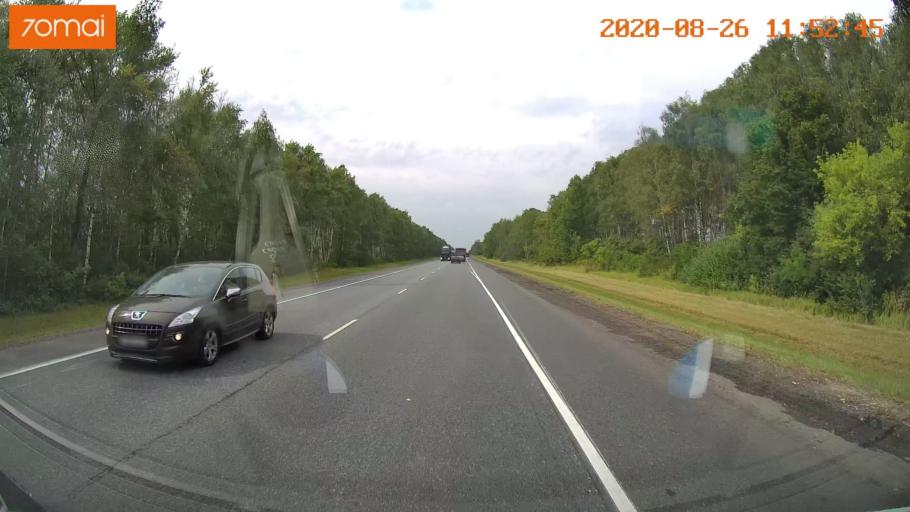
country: RU
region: Rjazan
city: Lesnoy
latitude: 54.2930
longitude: 40.4461
